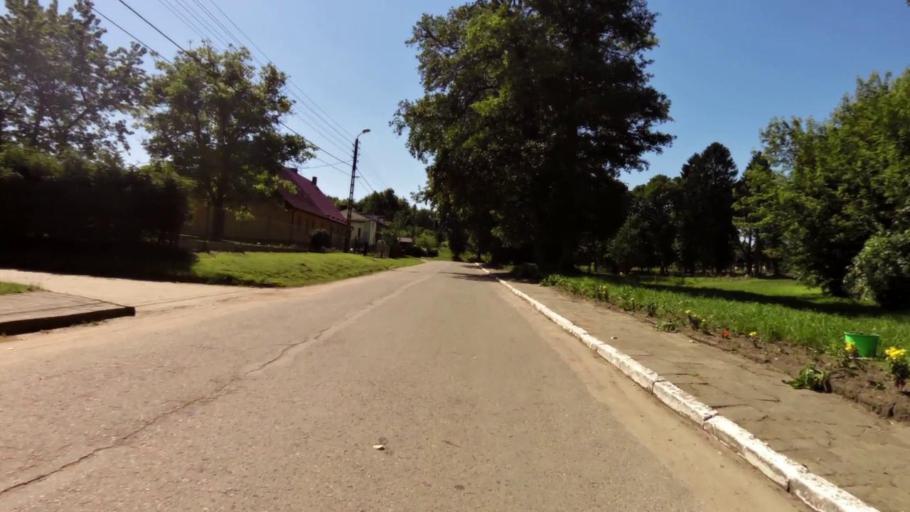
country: PL
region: West Pomeranian Voivodeship
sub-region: Powiat swidwinski
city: Rabino
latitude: 53.8868
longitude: 16.0118
